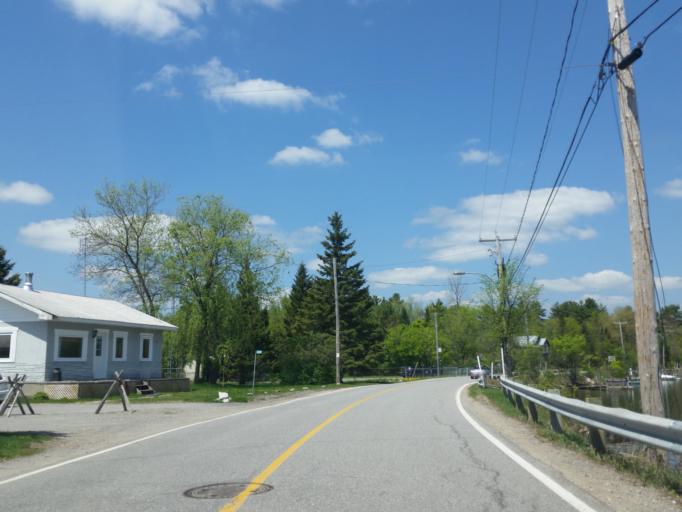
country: CA
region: Quebec
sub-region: Outaouais
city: Wakefield
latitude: 45.6028
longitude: -75.8886
